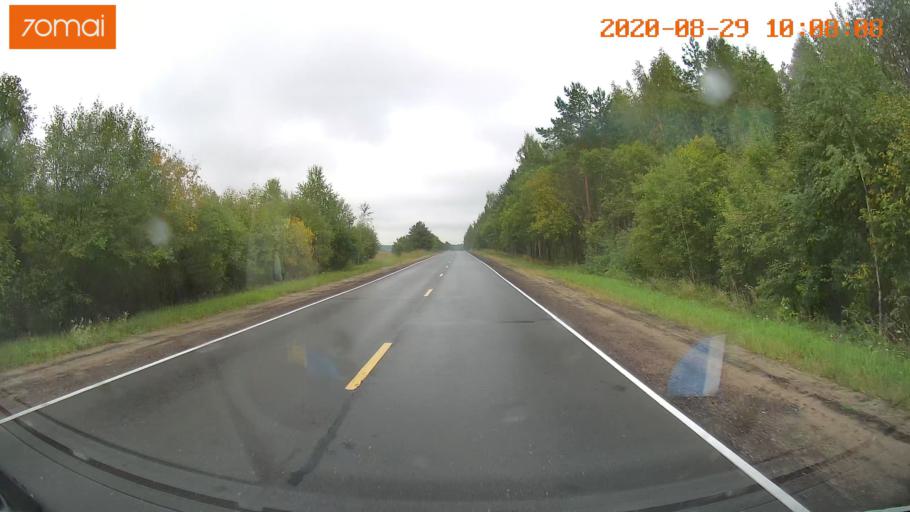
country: RU
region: Ivanovo
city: Kuznechikha
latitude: 57.3770
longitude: 42.5824
